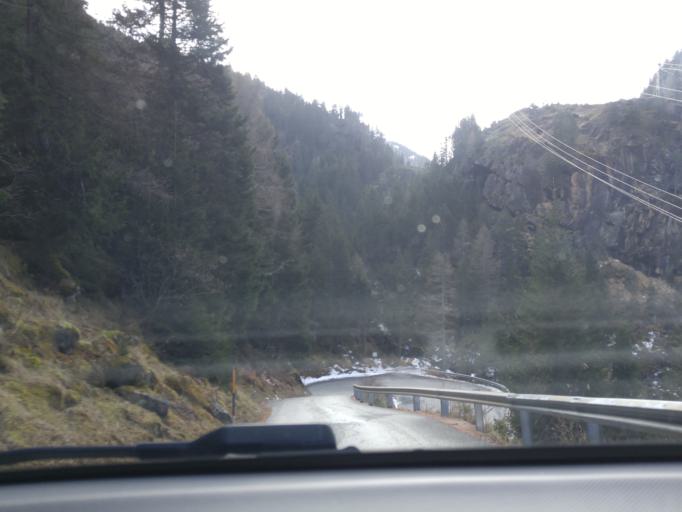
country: AT
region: Salzburg
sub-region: Politischer Bezirk Zell am See
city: Niedernsill
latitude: 47.1819
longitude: 12.6265
